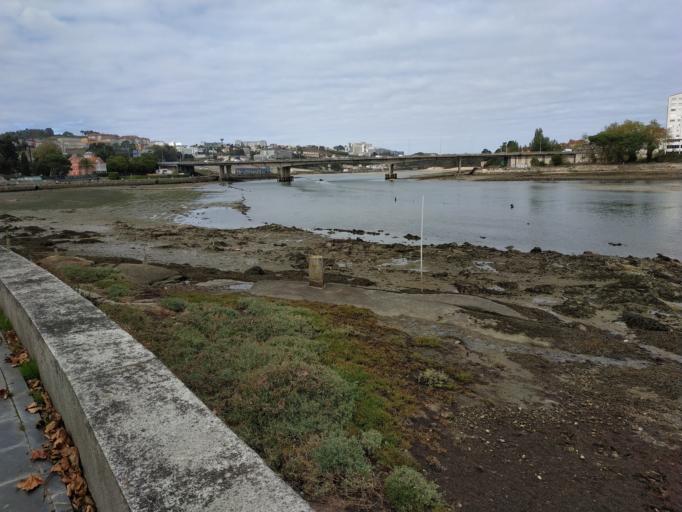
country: ES
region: Galicia
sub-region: Provincia da Coruna
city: Culleredo
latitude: 43.3294
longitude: -8.3797
